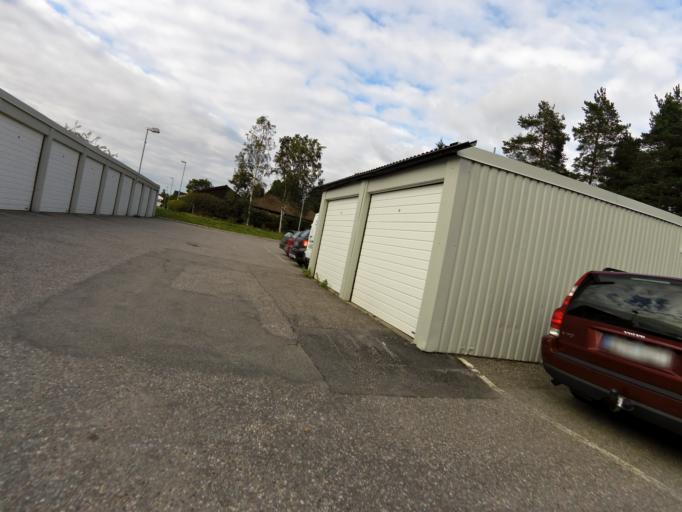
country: SE
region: Gaevleborg
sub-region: Gavle Kommun
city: Gavle
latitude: 60.6693
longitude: 17.2145
